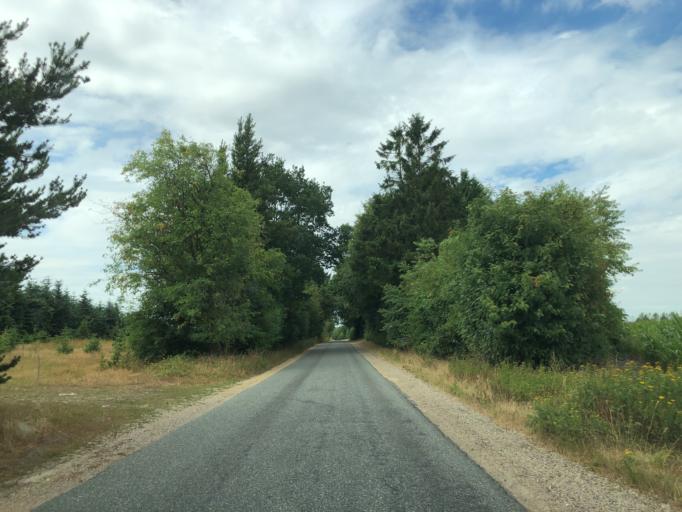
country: DK
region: South Denmark
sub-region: Billund Kommune
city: Grindsted
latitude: 55.6451
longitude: 8.9260
